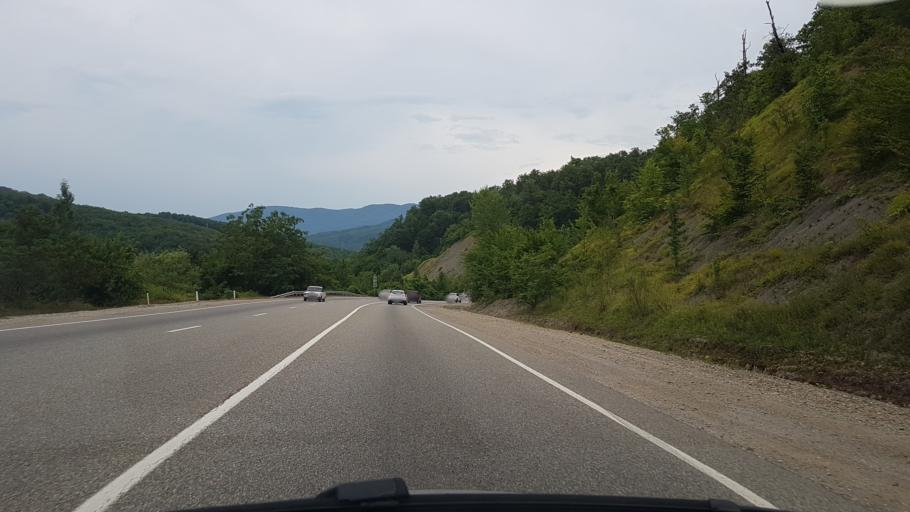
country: RU
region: Krasnodarskiy
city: Novomikhaylovskiy
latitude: 44.4924
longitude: 38.8983
